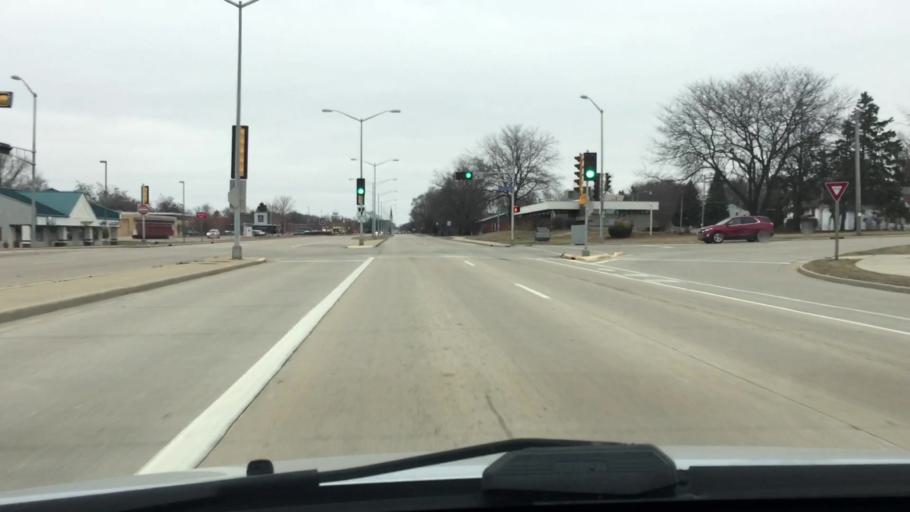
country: US
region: Wisconsin
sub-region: Jefferson County
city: Watertown
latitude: 43.1742
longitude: -88.7319
